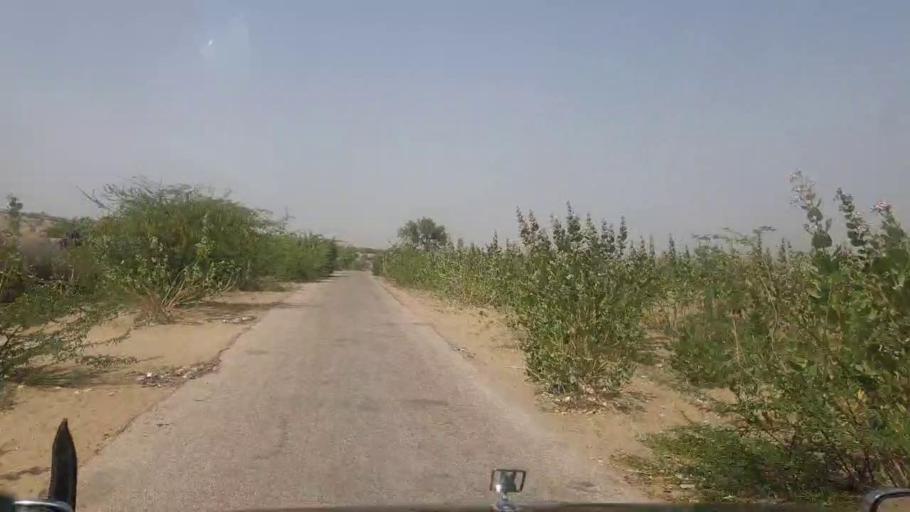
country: PK
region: Sindh
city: Islamkot
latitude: 25.1268
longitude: 70.2224
